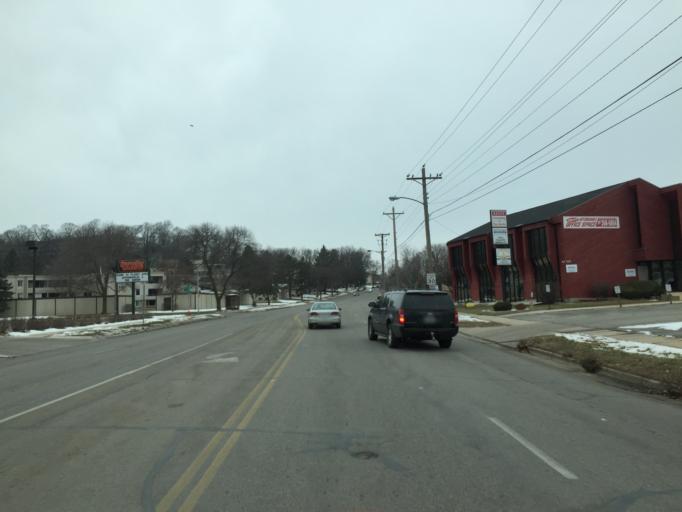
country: US
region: Minnesota
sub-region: Olmsted County
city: Rochester
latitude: 44.0446
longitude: -92.4678
